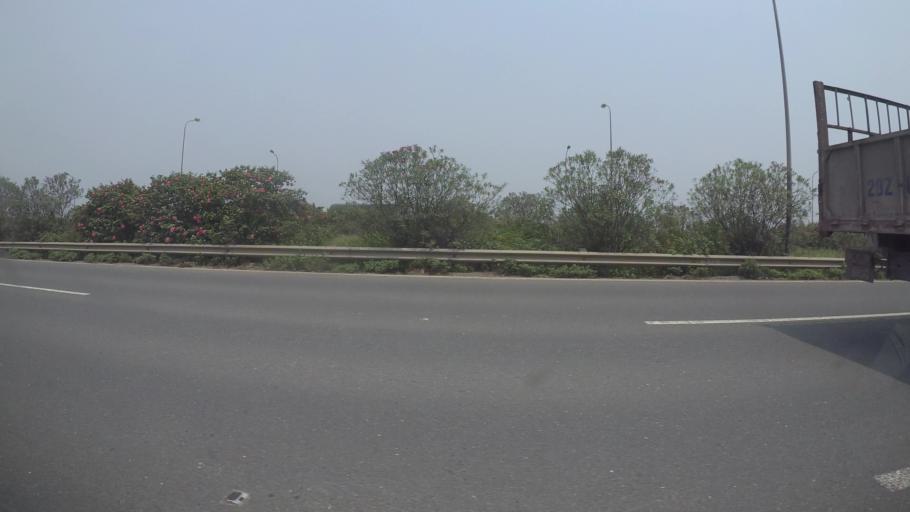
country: VN
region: Ha Noi
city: Quoc Oai
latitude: 21.0012
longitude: 105.6133
